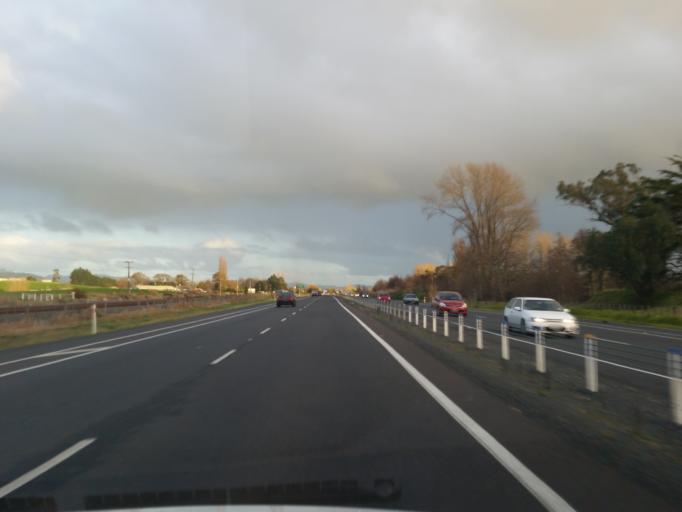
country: NZ
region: Waikato
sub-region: Waikato District
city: Te Kauwhata
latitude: -37.4646
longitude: 175.1572
